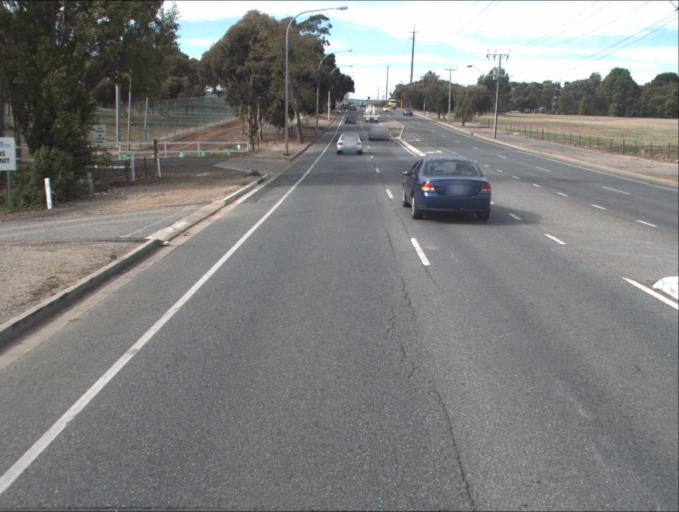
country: AU
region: South Australia
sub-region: Port Adelaide Enfield
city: Gilles Plains
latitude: -34.8466
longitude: 138.6385
